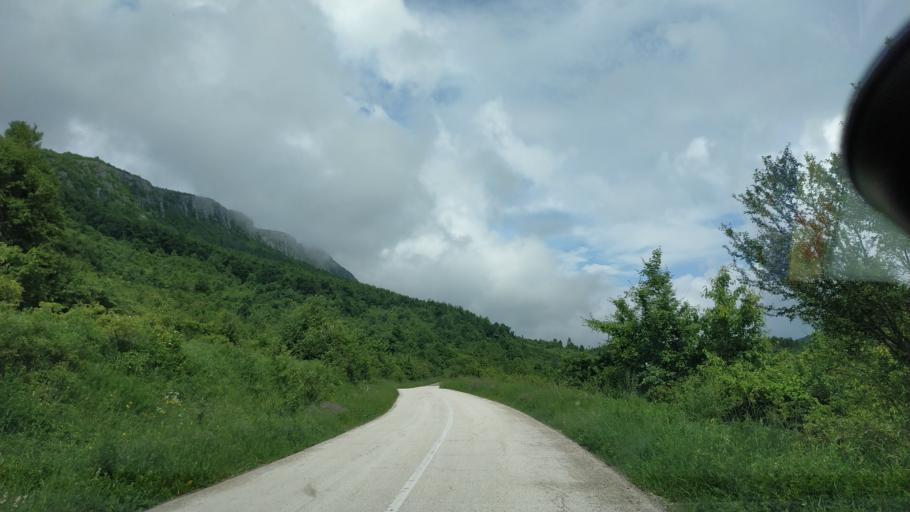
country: RS
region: Central Serbia
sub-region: Zajecarski Okrug
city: Boljevac
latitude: 43.7498
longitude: 21.9453
